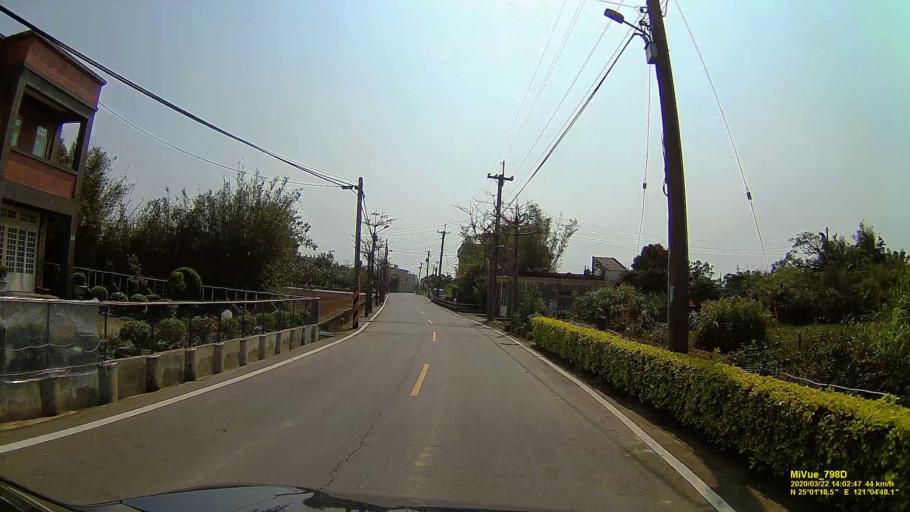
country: TW
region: Taiwan
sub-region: Hsinchu
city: Zhubei
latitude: 25.0215
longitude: 121.0796
